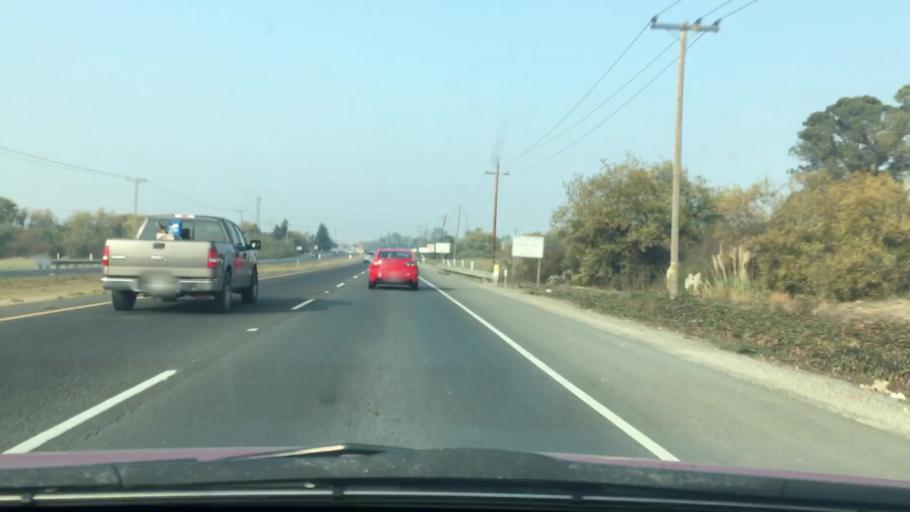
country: US
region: California
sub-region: Napa County
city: American Canyon
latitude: 38.1608
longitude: -122.2531
